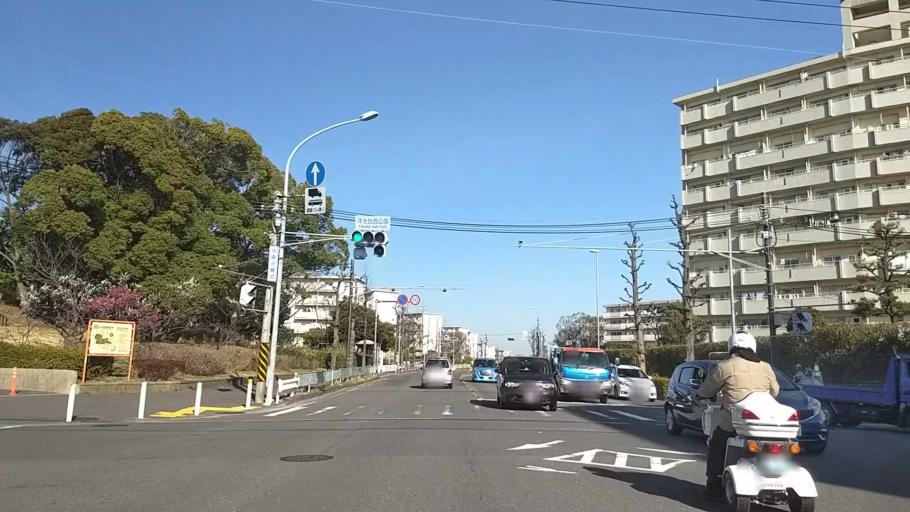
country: JP
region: Kanagawa
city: Yokohama
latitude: 35.3811
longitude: 139.5938
